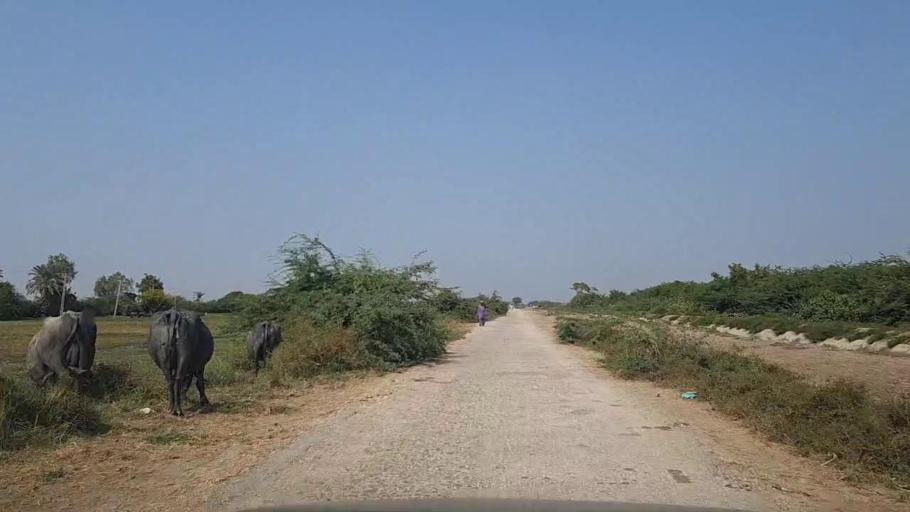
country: PK
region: Sindh
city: Chuhar Jamali
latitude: 24.5213
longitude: 67.9261
